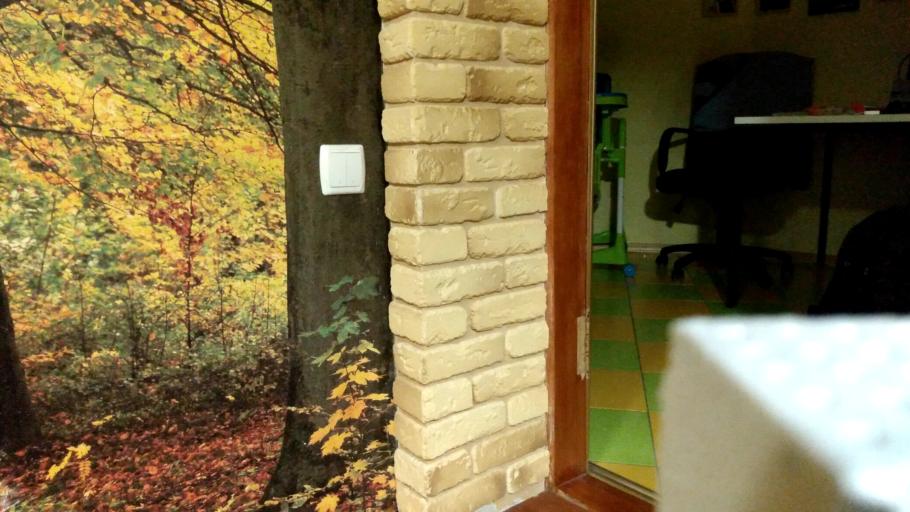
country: RU
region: Arkhangelskaya
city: Kargopol'
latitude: 61.5673
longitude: 37.7558
